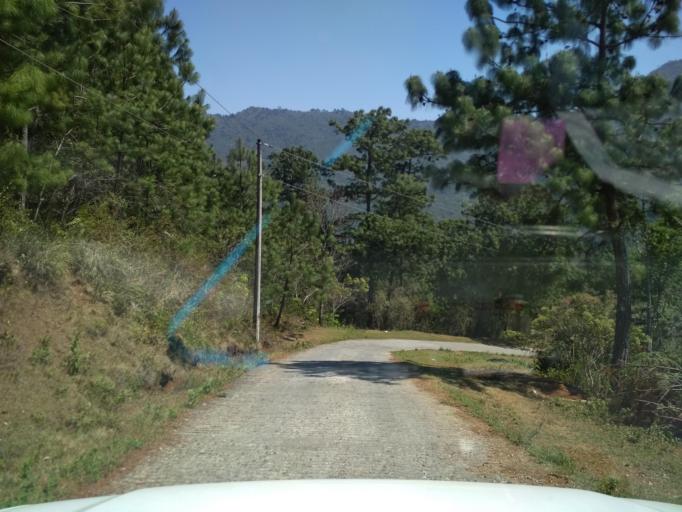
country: MX
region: Veracruz
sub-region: Tlilapan
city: Tonalixco
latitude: 18.7716
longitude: -97.0856
